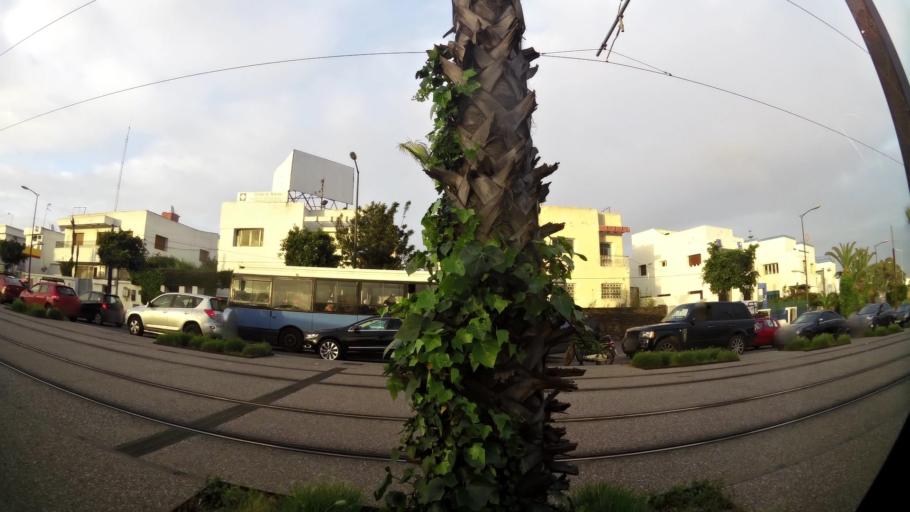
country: MA
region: Grand Casablanca
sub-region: Casablanca
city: Casablanca
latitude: 33.5707
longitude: -7.6687
